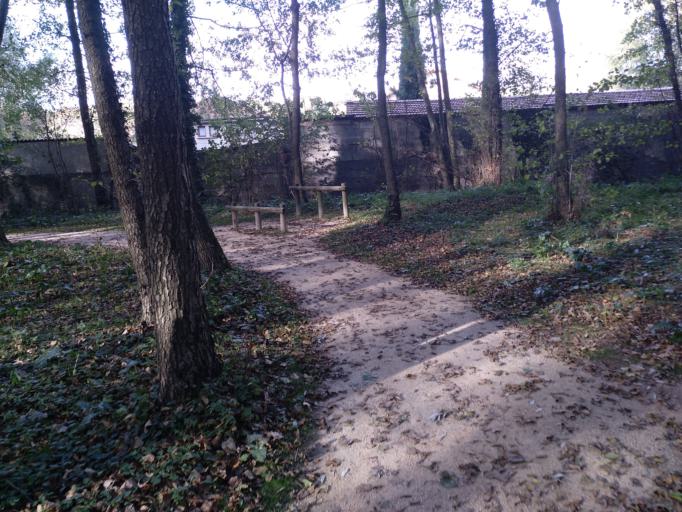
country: FR
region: Rhone-Alpes
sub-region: Departement du Rhone
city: Chaponnay
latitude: 45.6376
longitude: 4.9339
